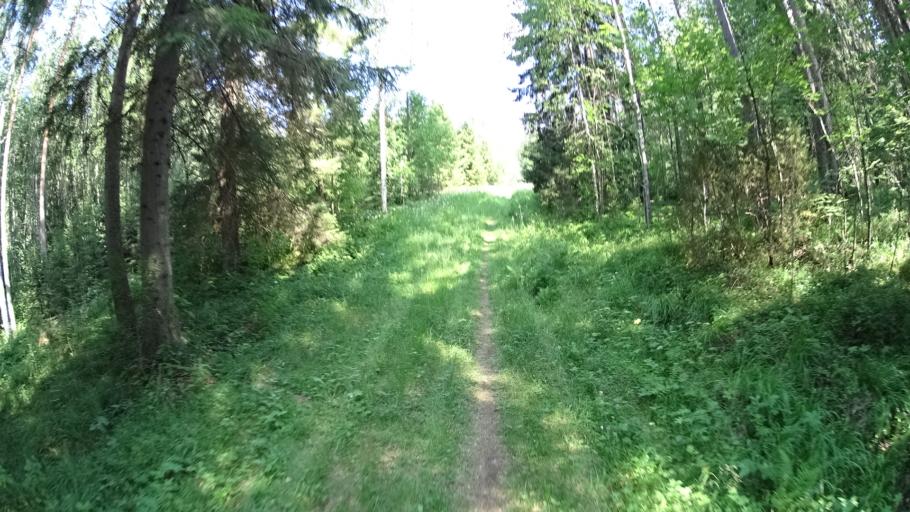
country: FI
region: North Karelia
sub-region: Pielisen Karjala
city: Lieksa
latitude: 63.1214
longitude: 29.8046
